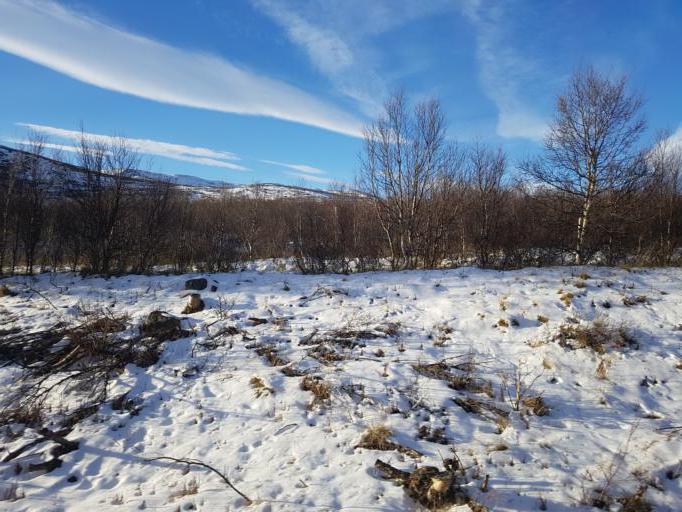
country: NO
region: Oppland
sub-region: Dovre
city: Dovre
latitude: 62.2251
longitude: 9.5374
